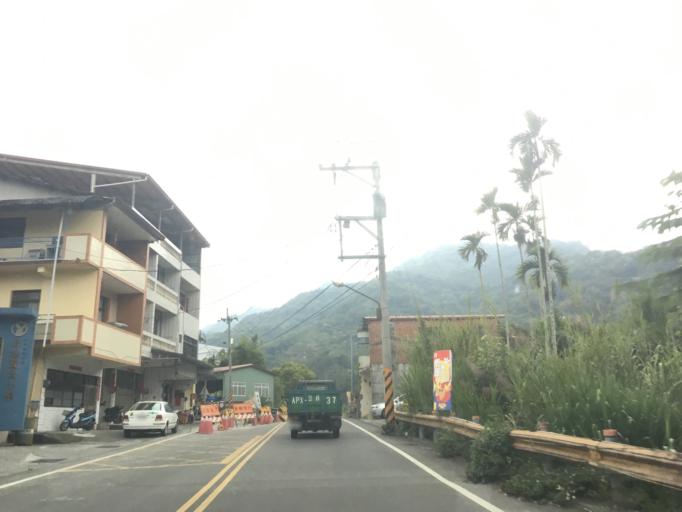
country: TW
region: Taiwan
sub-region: Nantou
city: Puli
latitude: 23.9507
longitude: 120.8691
